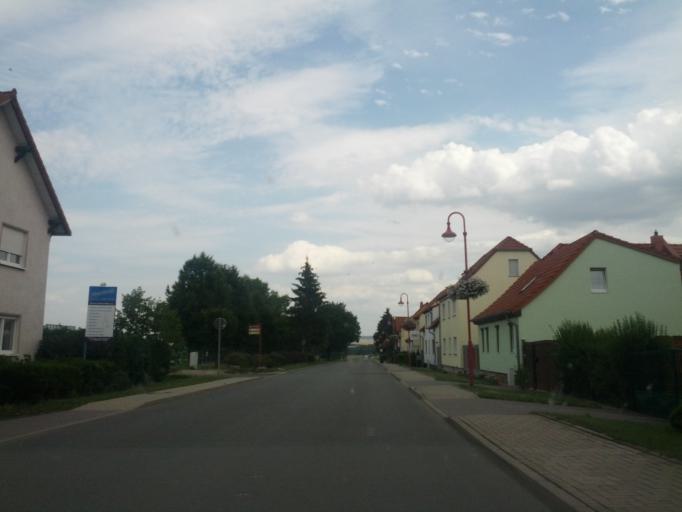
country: DE
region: Thuringia
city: Ichtershausen
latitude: 50.8868
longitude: 10.9461
